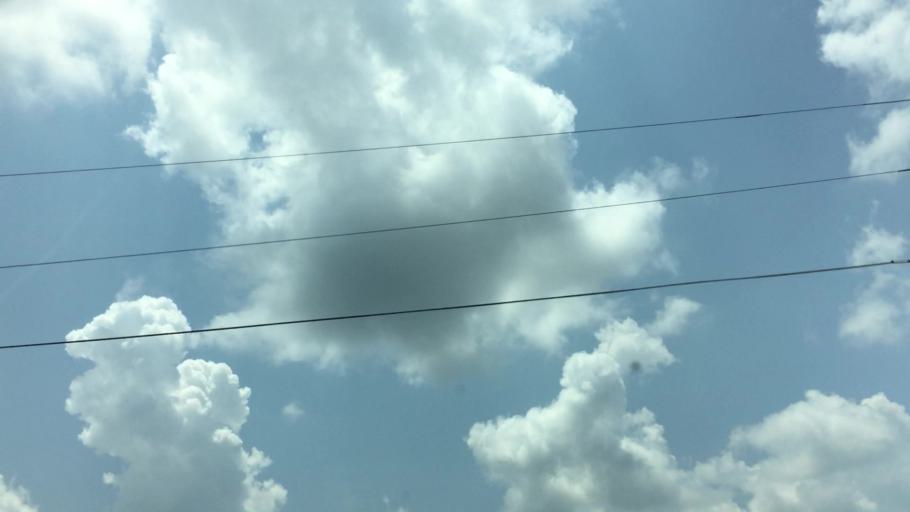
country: US
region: Georgia
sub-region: Carroll County
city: Carrollton
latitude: 33.6080
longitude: -85.0168
